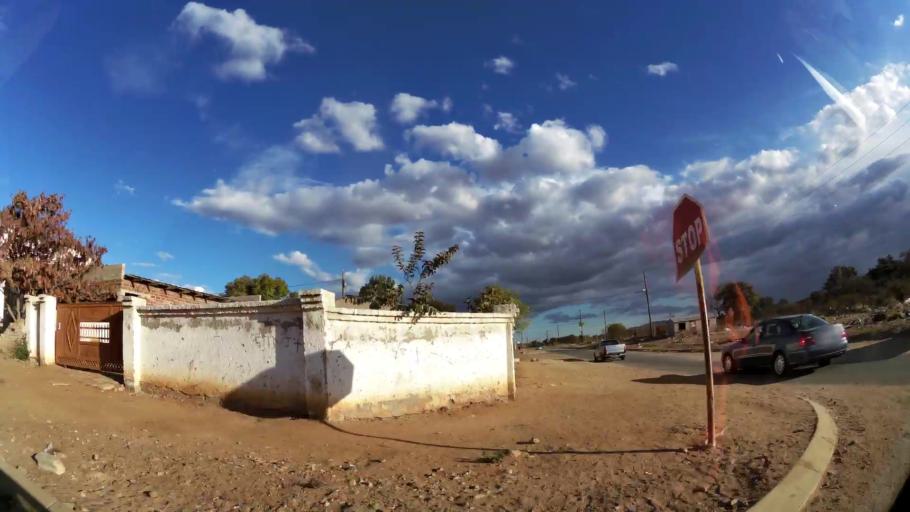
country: ZA
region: Limpopo
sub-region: Capricorn District Municipality
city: Polokwane
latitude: -23.9111
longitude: 29.4240
